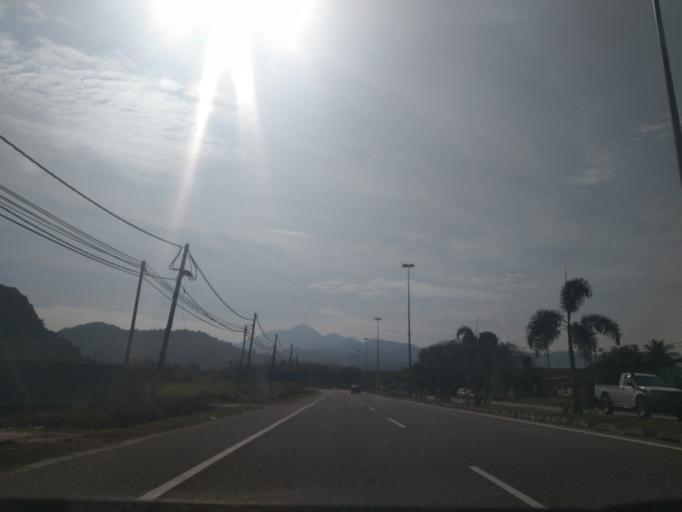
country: MY
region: Perak
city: Ipoh
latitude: 4.5020
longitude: 101.1443
